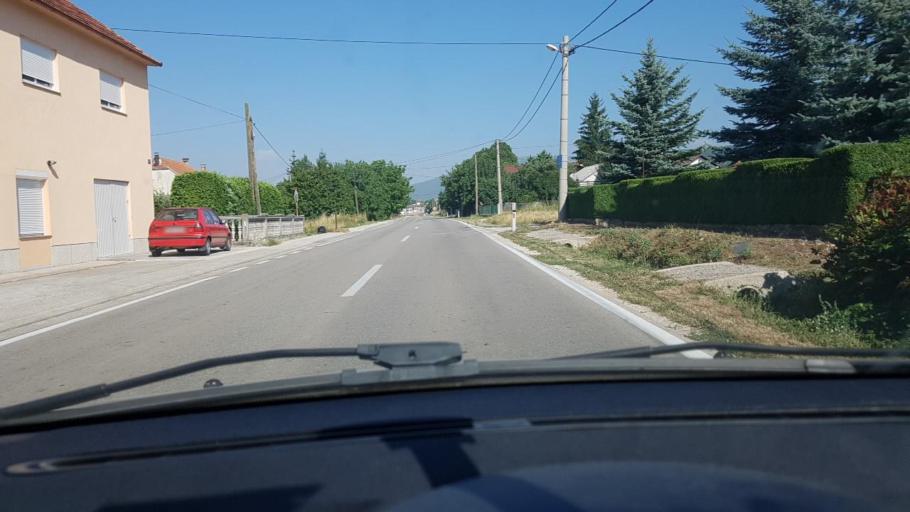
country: BA
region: Federation of Bosnia and Herzegovina
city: Livno
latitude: 43.8383
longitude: 16.9773
